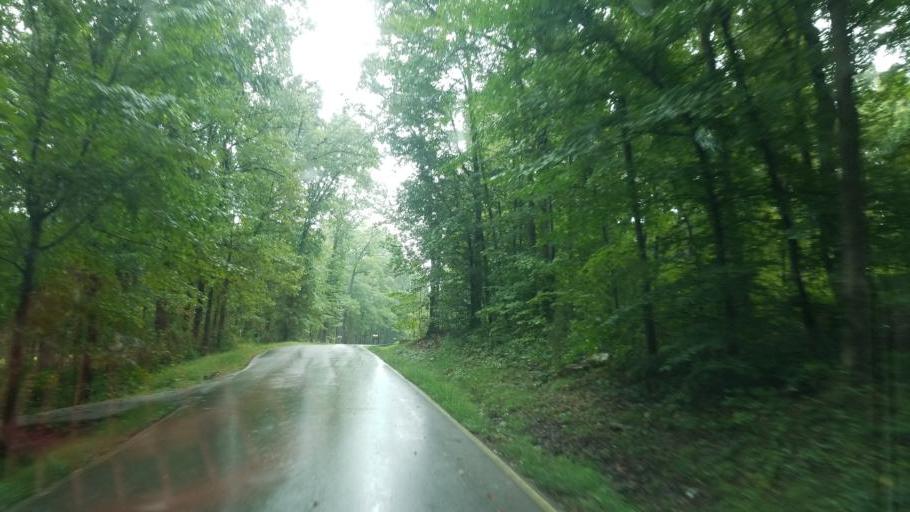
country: US
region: Kentucky
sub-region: Rowan County
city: Morehead
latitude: 38.1759
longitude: -83.4939
